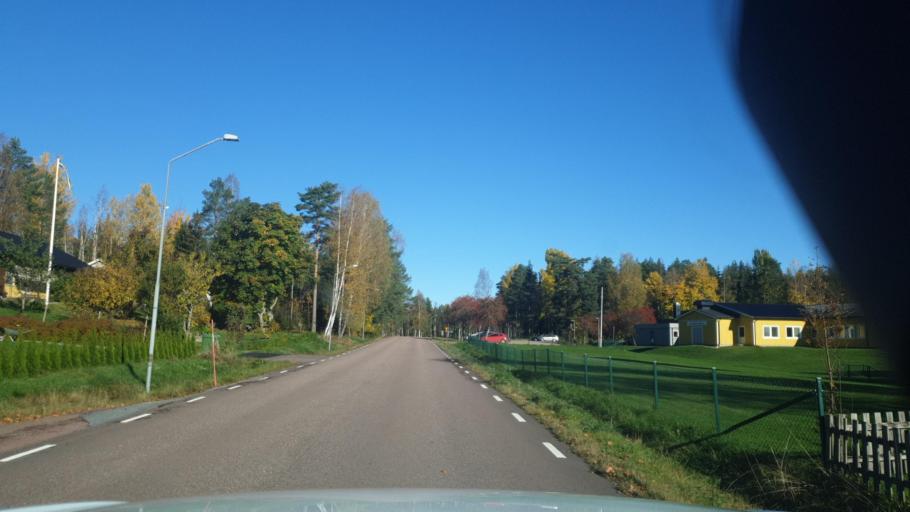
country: SE
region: Vaermland
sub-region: Arvika Kommun
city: Arvika
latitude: 59.5398
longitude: 12.7451
